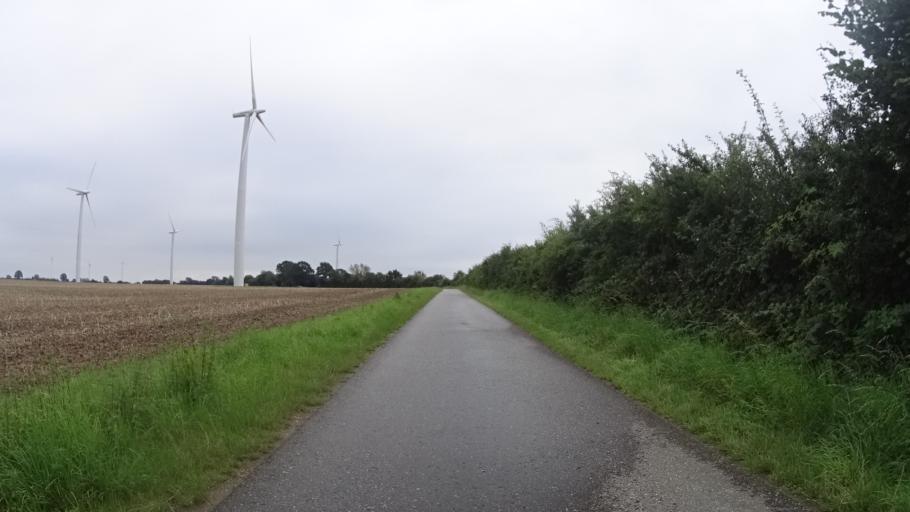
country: DE
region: Schleswig-Holstein
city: Stubben
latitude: 53.7156
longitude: 10.4244
